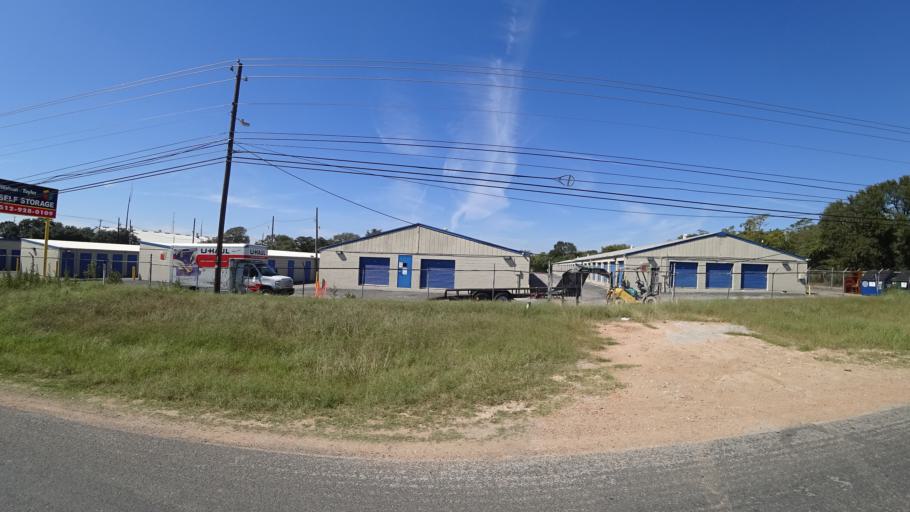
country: US
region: Texas
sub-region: Travis County
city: Austin
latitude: 30.2680
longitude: -97.6708
